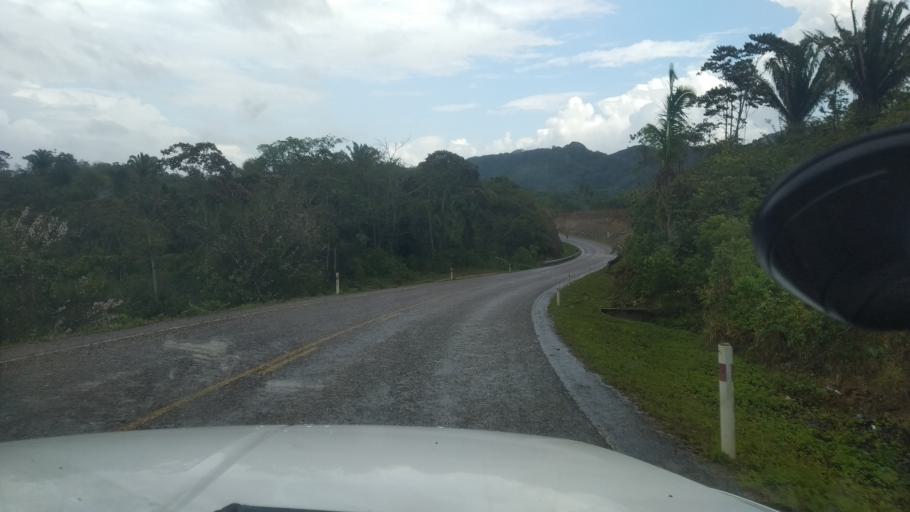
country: GT
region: Peten
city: San Luis
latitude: 16.1848
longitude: -89.2057
